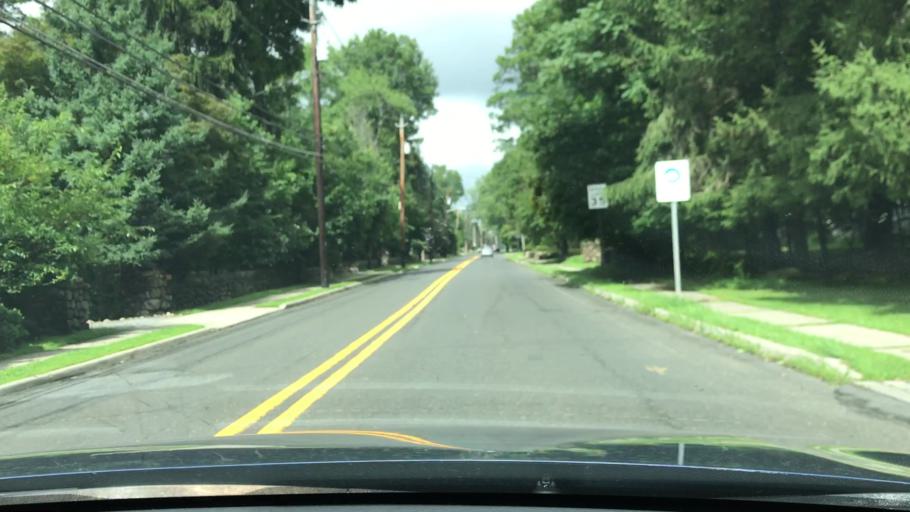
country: US
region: New Jersey
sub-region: Bergen County
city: Ramsey
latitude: 41.0430
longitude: -74.1622
